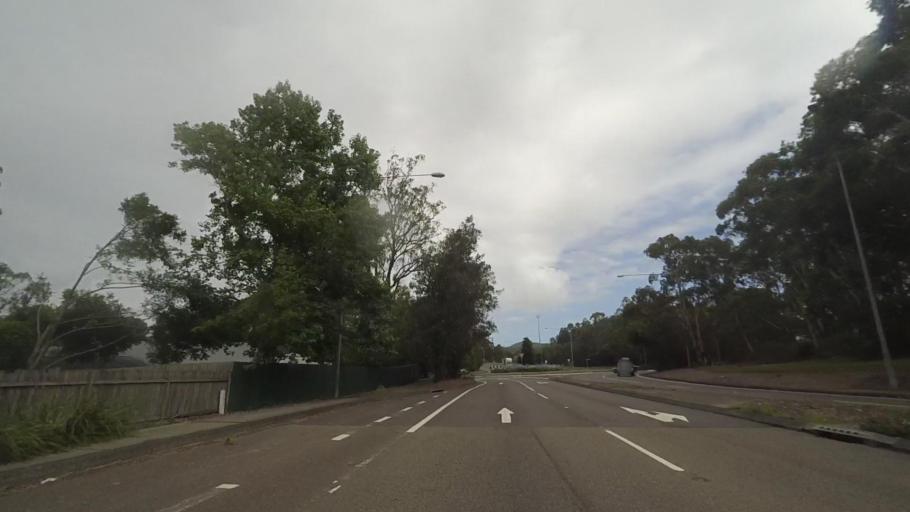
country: AU
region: New South Wales
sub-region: Wyong Shire
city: Berkeley Vale
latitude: -33.3565
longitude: 151.4399
